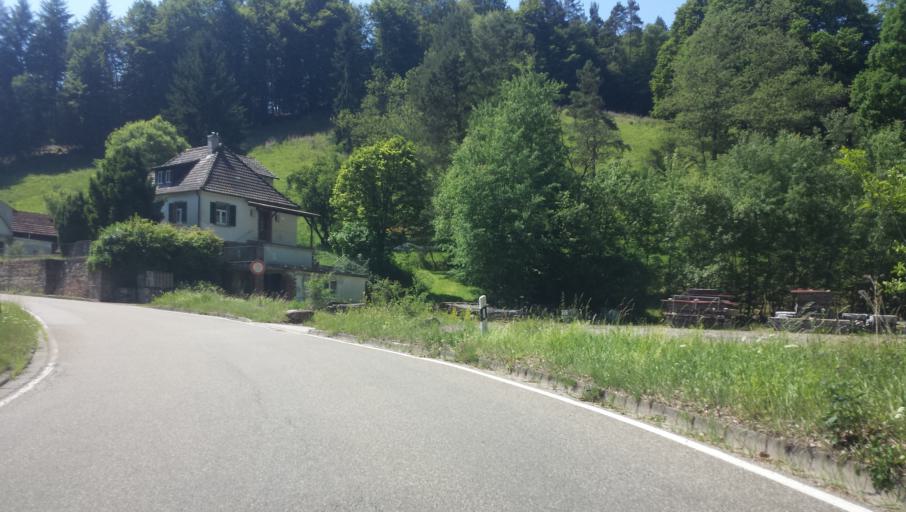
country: DE
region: Rheinland-Pfalz
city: Waldleiningen
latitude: 49.3552
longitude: 7.8838
